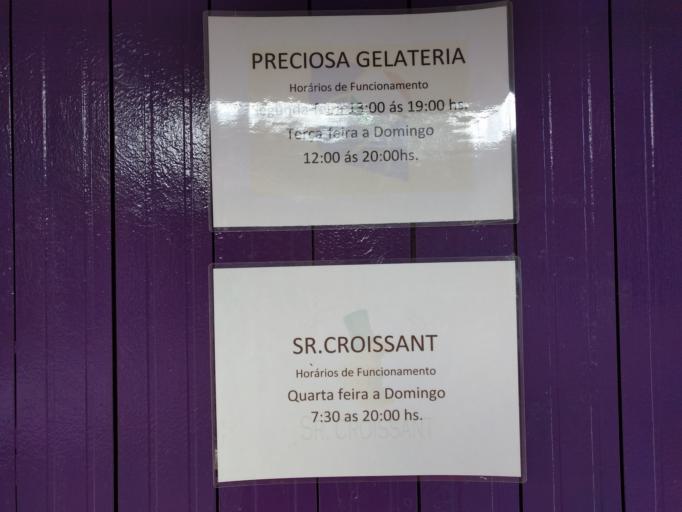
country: BR
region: Rio Grande do Norte
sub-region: Ares
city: Ares
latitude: -6.2297
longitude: -35.0469
